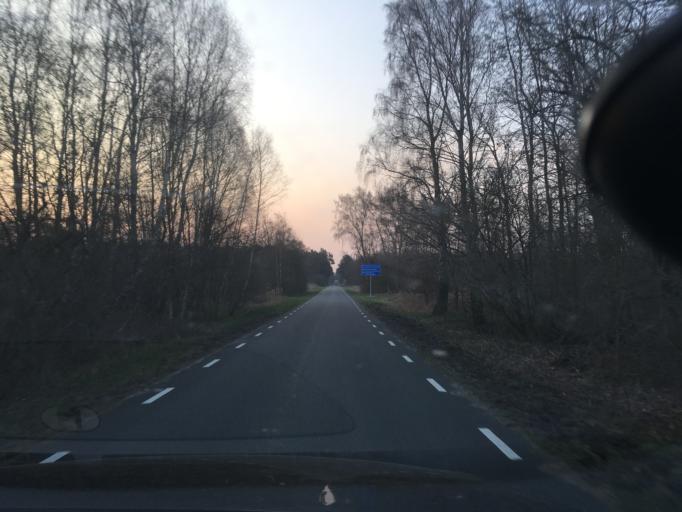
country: SE
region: Skane
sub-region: Simrishamns Kommun
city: Simrishamn
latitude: 55.3972
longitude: 14.1722
